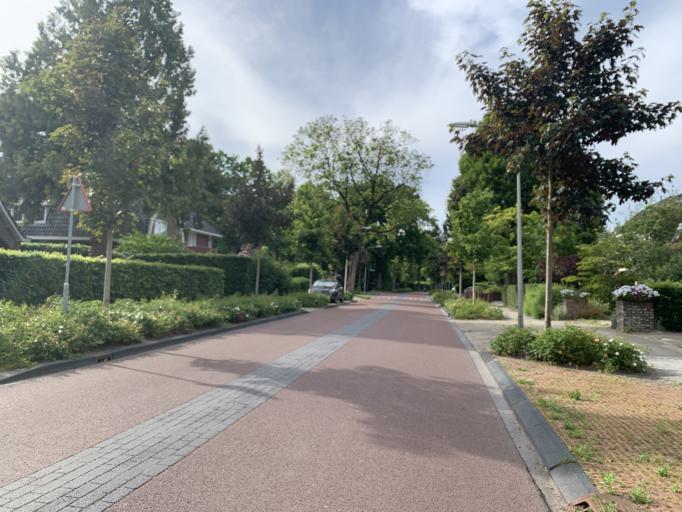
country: NL
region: Groningen
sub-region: Gemeente Haren
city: Haren
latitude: 53.1710
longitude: 6.6116
